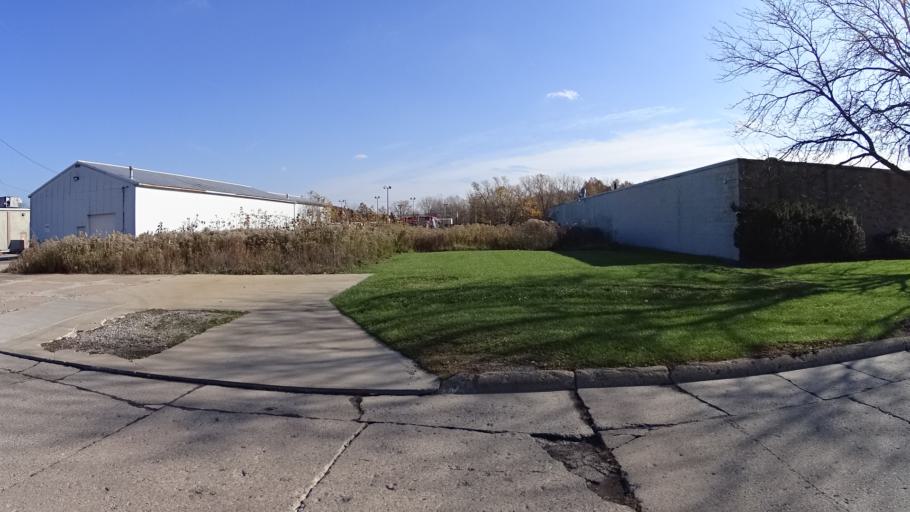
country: US
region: Ohio
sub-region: Lorain County
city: Lorain
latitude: 41.4644
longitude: -82.1591
